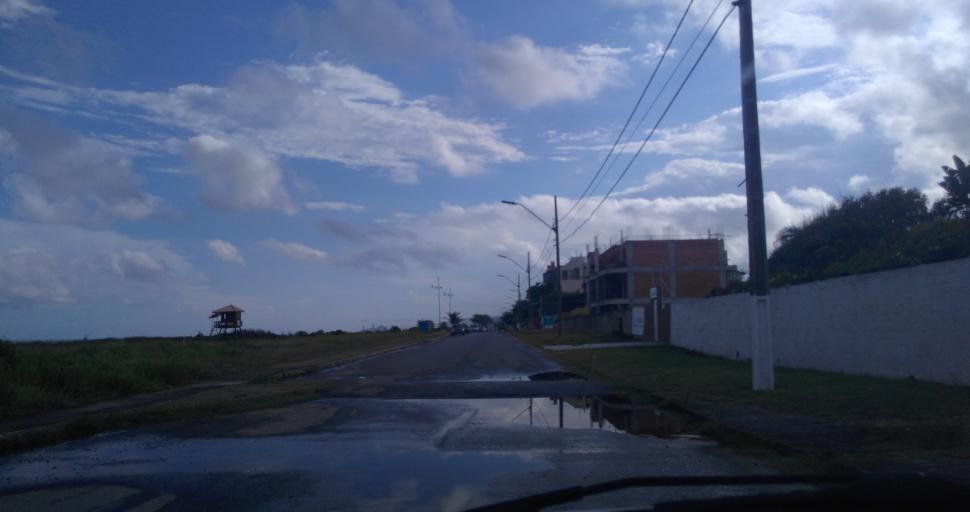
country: BR
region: Parana
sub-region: Pontal Do Parana
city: Pontal do Parana
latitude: -25.7357
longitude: -48.4919
